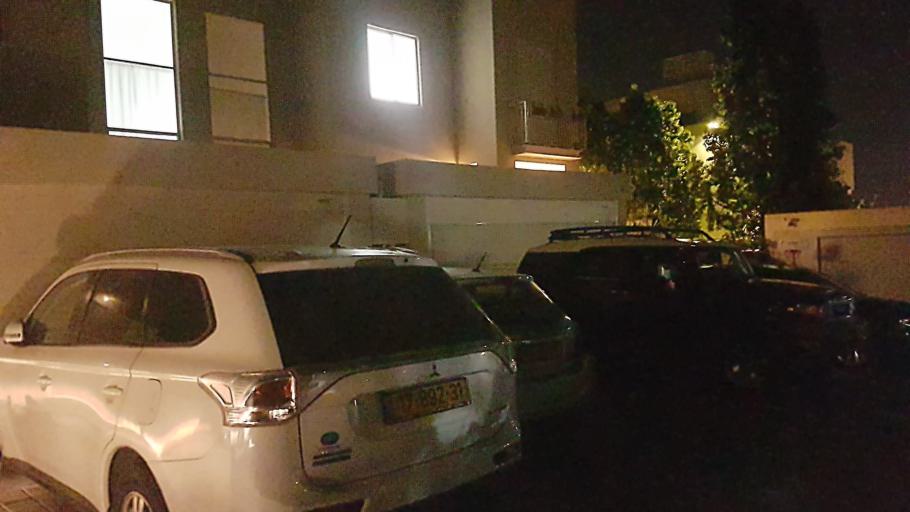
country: IL
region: Central District
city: Hod HaSharon
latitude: 32.1667
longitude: 34.8908
